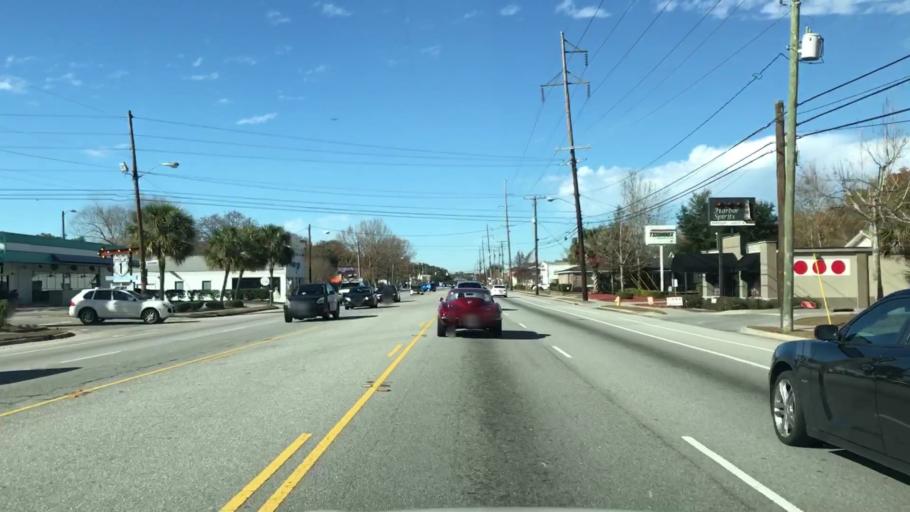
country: US
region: South Carolina
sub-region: Charleston County
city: Charleston
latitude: 32.7904
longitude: -79.9862
